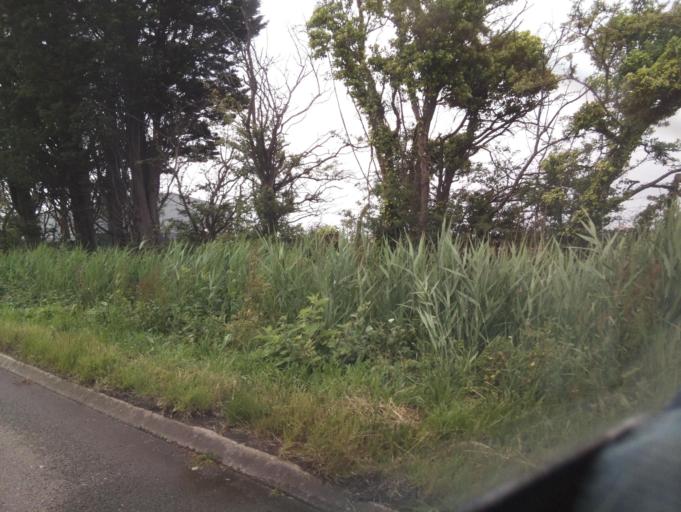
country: GB
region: Wales
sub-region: Vale of Glamorgan
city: Dinas Powys
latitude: 51.4118
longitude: -3.2293
